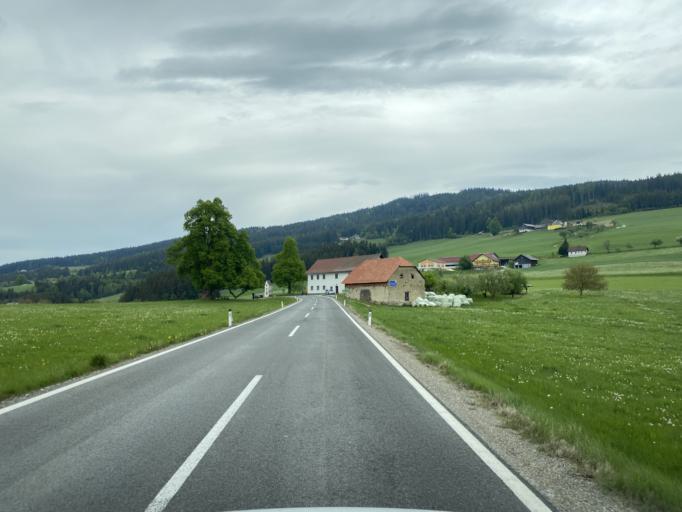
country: AT
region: Styria
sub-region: Politischer Bezirk Weiz
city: Gschaid bei Birkfeld
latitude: 47.3385
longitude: 15.7462
